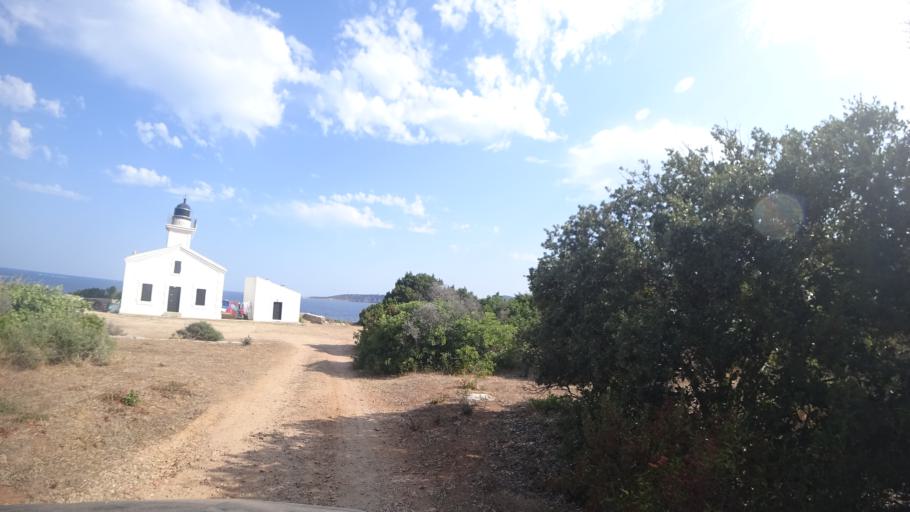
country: FR
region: Corsica
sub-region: Departement de la Corse-du-Sud
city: Porto-Vecchio
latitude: 41.6179
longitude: 9.3548
